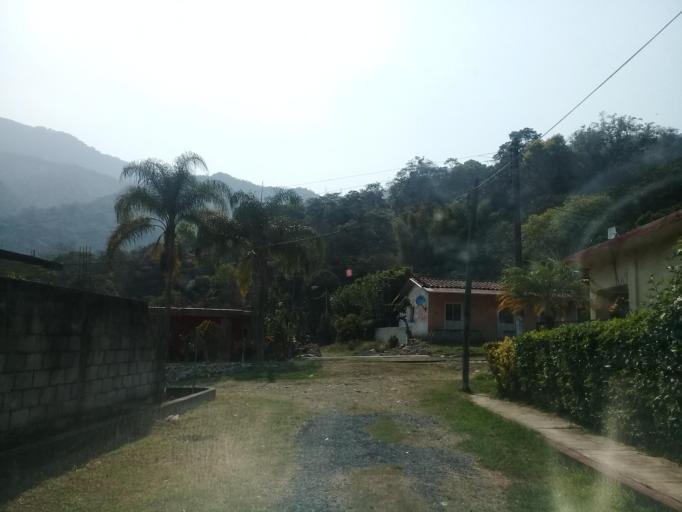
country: MX
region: Veracruz
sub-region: Ixtaczoquitlan
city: Campo Chico
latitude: 18.8392
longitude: -97.0303
